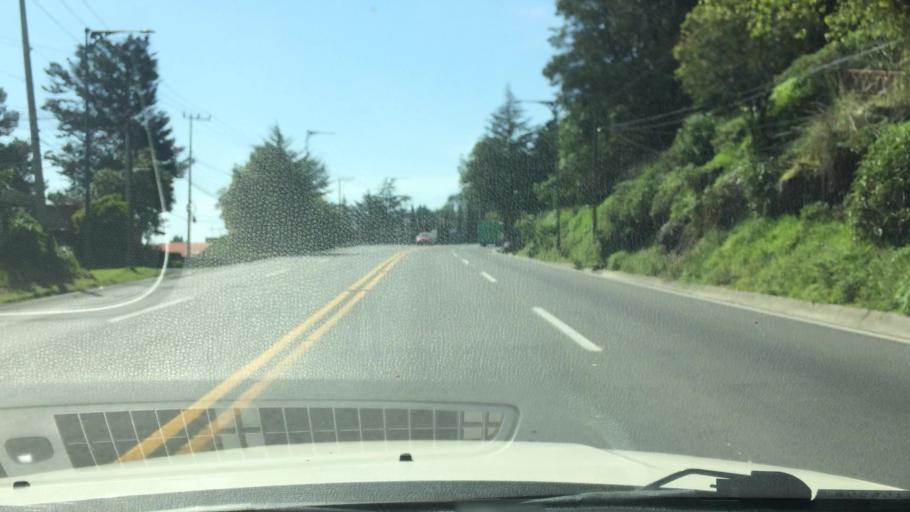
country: MX
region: Mexico City
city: Tlalpan
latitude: 19.2445
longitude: -99.1703
